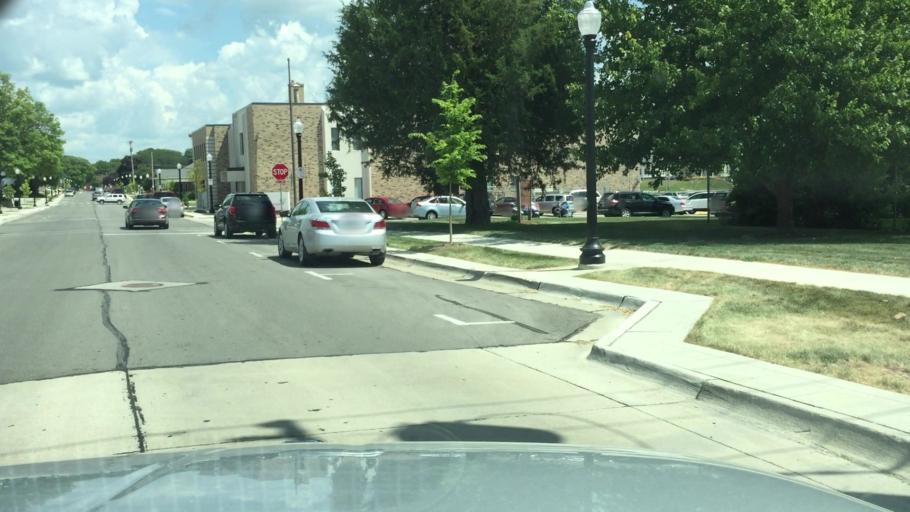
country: US
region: Iowa
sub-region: Jasper County
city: Newton
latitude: 41.6985
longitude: -93.0555
